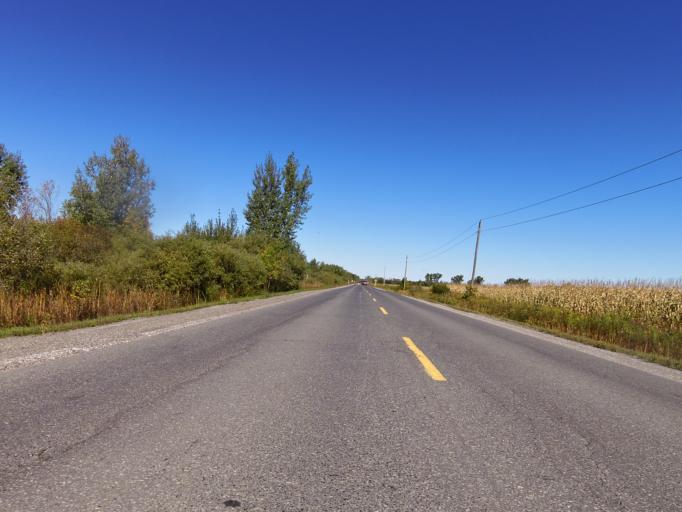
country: CA
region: Ontario
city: Clarence-Rockland
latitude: 45.3291
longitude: -75.4158
